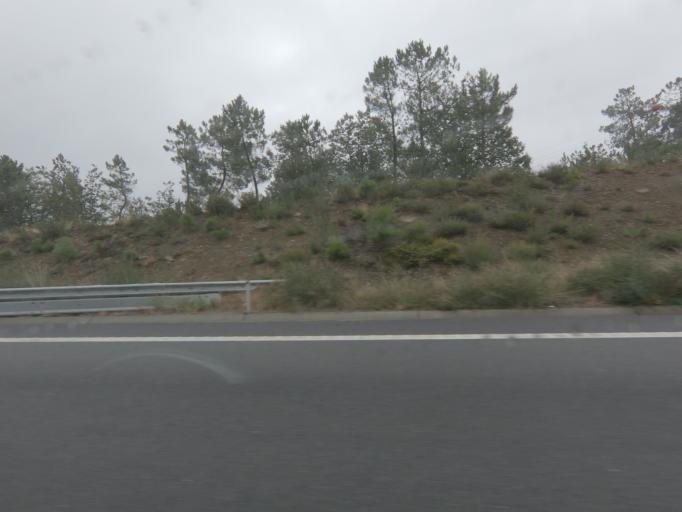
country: PT
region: Vila Real
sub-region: Santa Marta de Penaguiao
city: Santa Marta de Penaguiao
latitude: 41.2739
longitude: -7.8181
